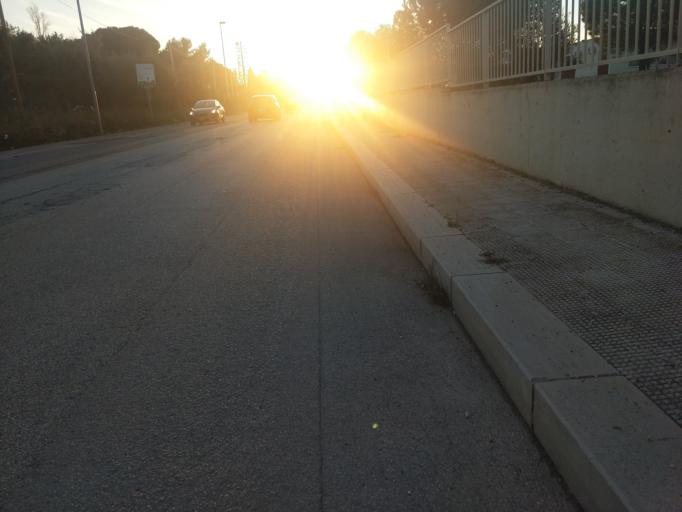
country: IT
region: Apulia
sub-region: Provincia di Bari
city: Modugno
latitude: 41.0838
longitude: 16.7987
